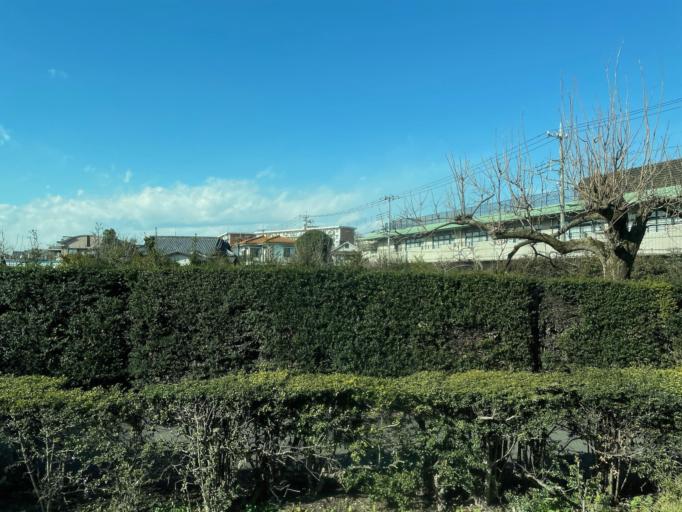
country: JP
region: Tokyo
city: Tanashicho
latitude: 35.7345
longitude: 139.5290
